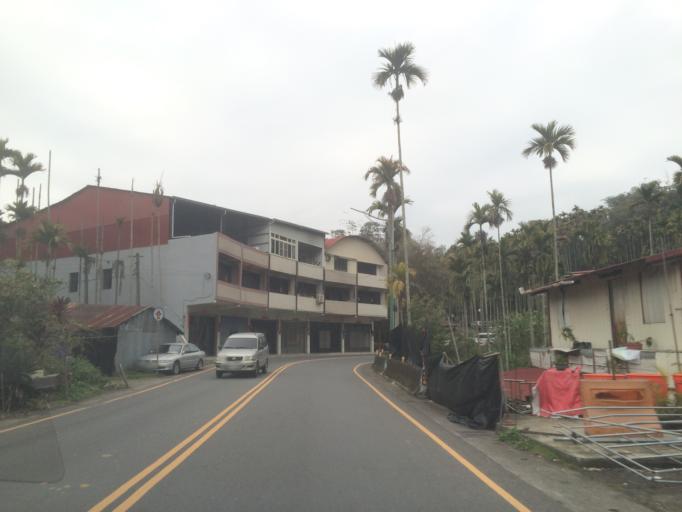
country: TW
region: Taiwan
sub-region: Nantou
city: Puli
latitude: 23.8669
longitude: 120.9026
